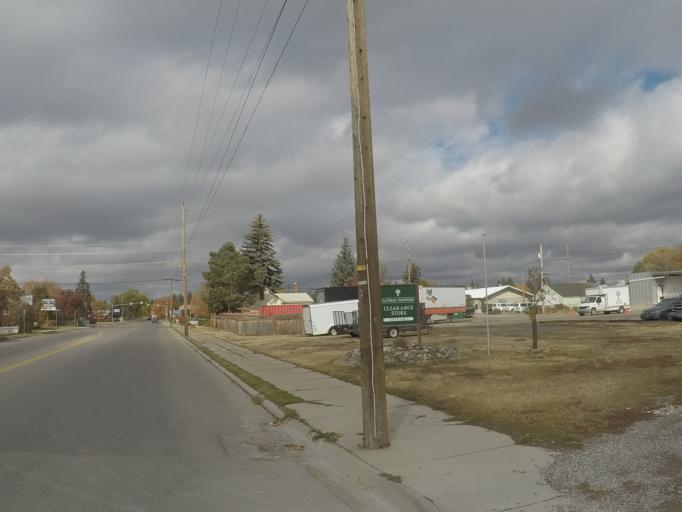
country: US
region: Montana
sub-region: Flathead County
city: Kalispell
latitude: 48.1988
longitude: -114.3214
